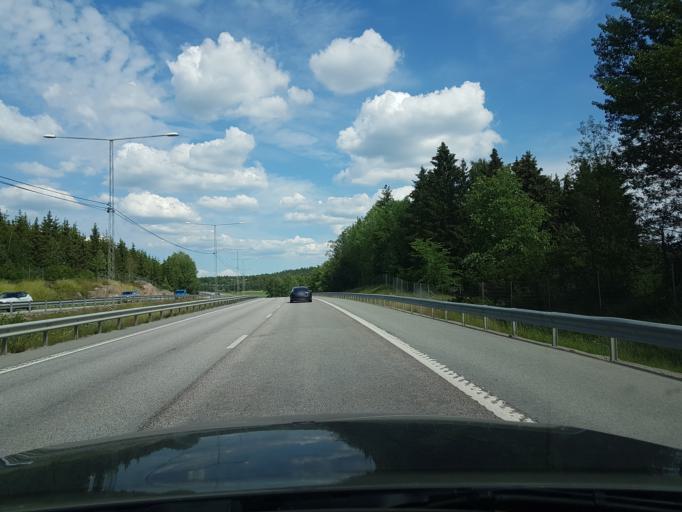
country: SE
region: Stockholm
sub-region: Taby Kommun
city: Taby
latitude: 59.4693
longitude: 18.1557
